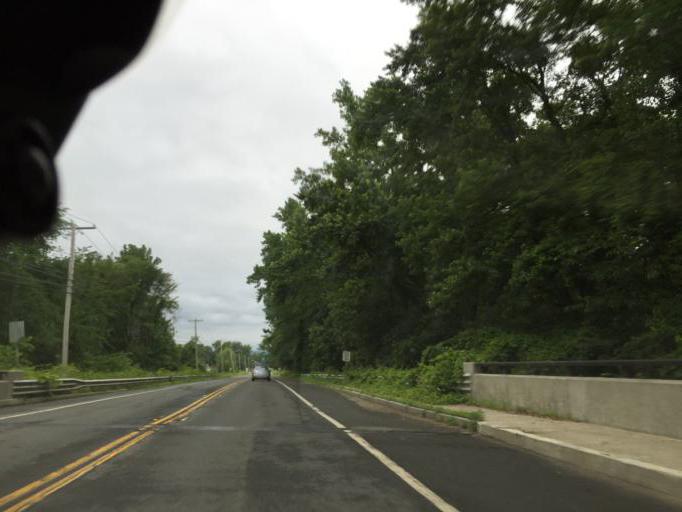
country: US
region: Massachusetts
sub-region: Berkshire County
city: Great Barrington
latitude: 42.1635
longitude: -73.3649
